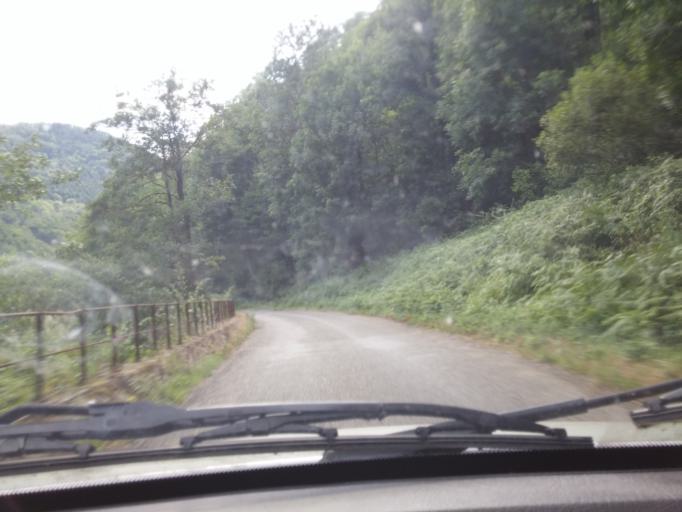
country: FR
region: Midi-Pyrenees
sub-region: Departement de l'Ariege
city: Saint-Girons
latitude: 42.9160
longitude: 1.2019
